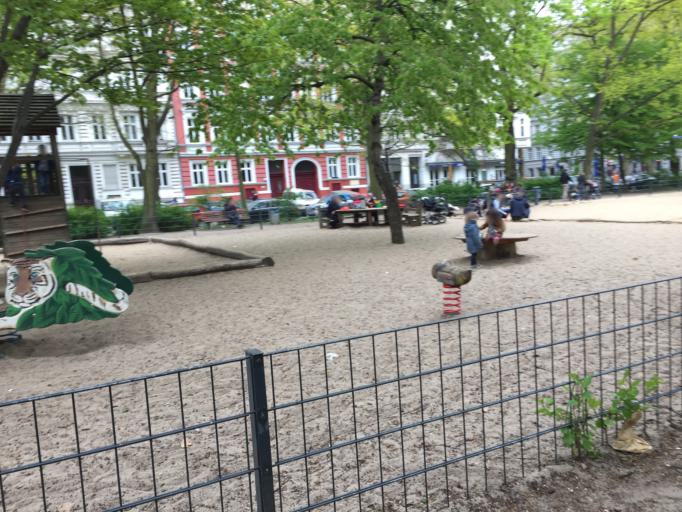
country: DE
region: Berlin
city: Bezirk Kreuzberg
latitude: 52.4939
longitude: 13.4142
